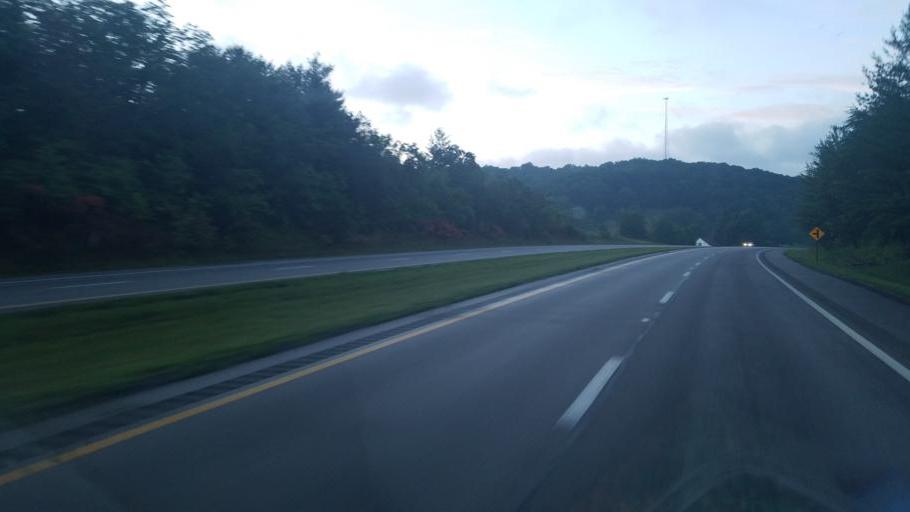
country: US
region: Ohio
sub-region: Jackson County
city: Jackson
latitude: 39.1833
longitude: -82.7539
